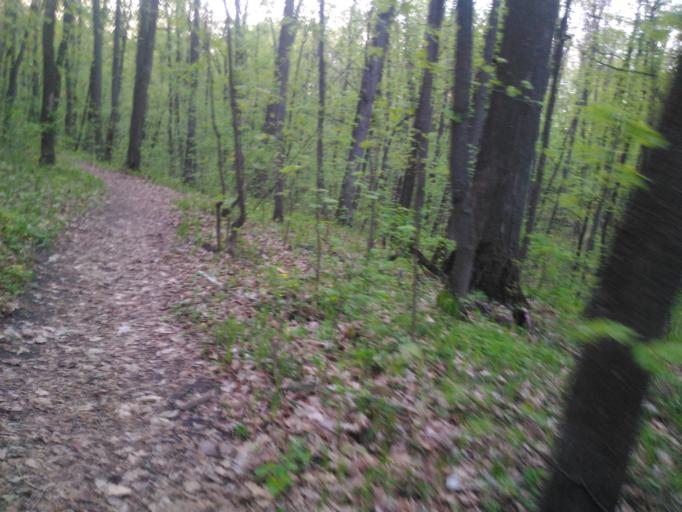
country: RU
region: Ulyanovsk
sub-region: Ulyanovskiy Rayon
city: Ulyanovsk
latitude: 54.2716
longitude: 48.3385
